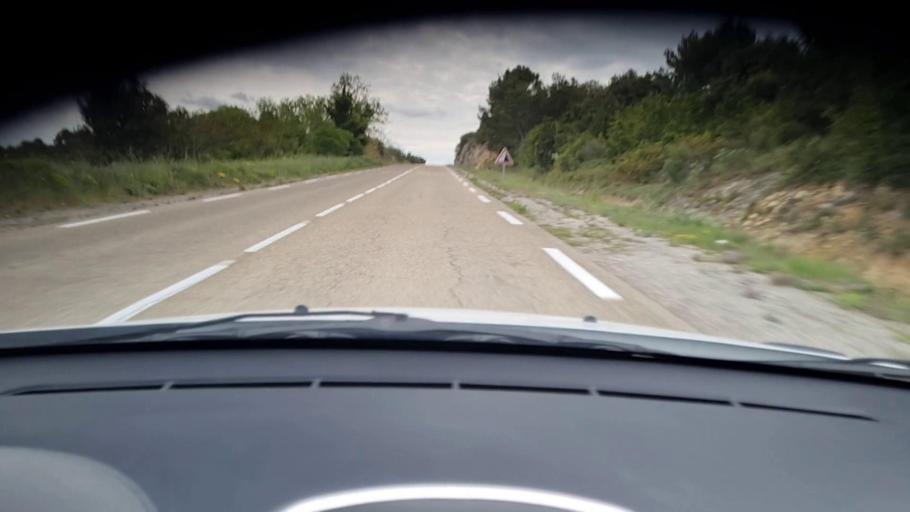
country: FR
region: Languedoc-Roussillon
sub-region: Departement du Gard
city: Poulx
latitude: 43.9101
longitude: 4.3899
